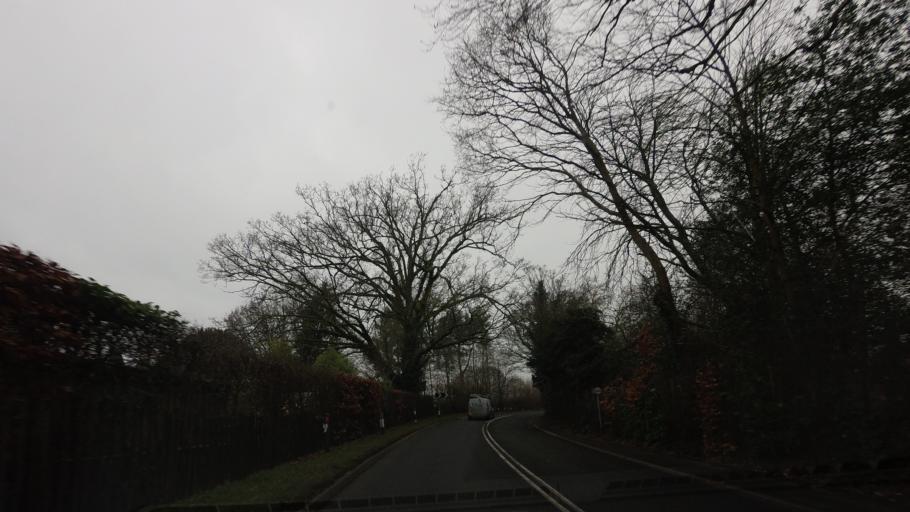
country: GB
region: England
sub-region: Kent
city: Hawkhurst
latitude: 51.0594
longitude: 0.5052
